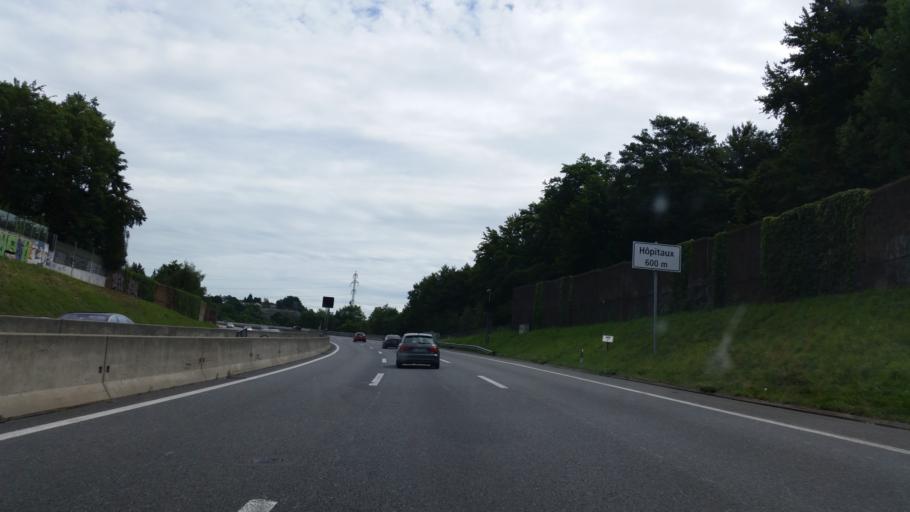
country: CH
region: Vaud
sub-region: Lausanne District
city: Blecherette
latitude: 46.5423
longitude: 6.6378
